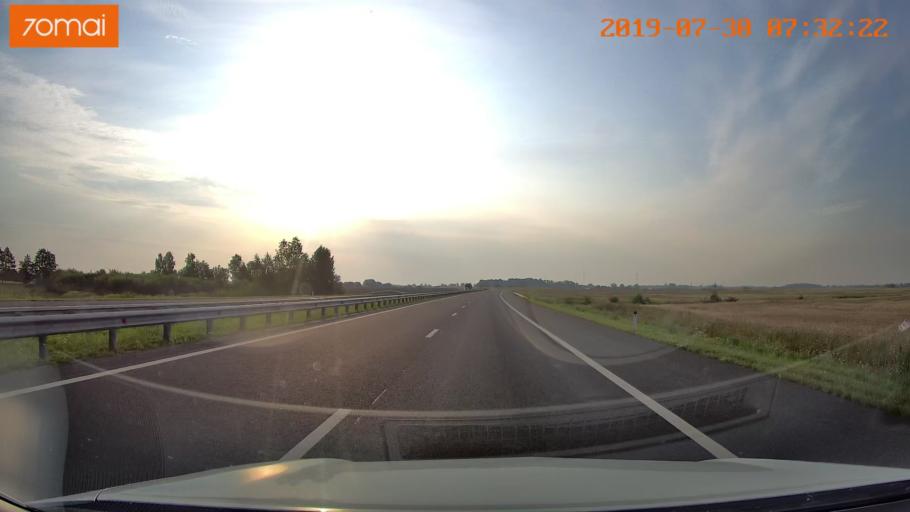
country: RU
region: Kaliningrad
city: Gvardeysk
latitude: 54.6673
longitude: 21.0186
